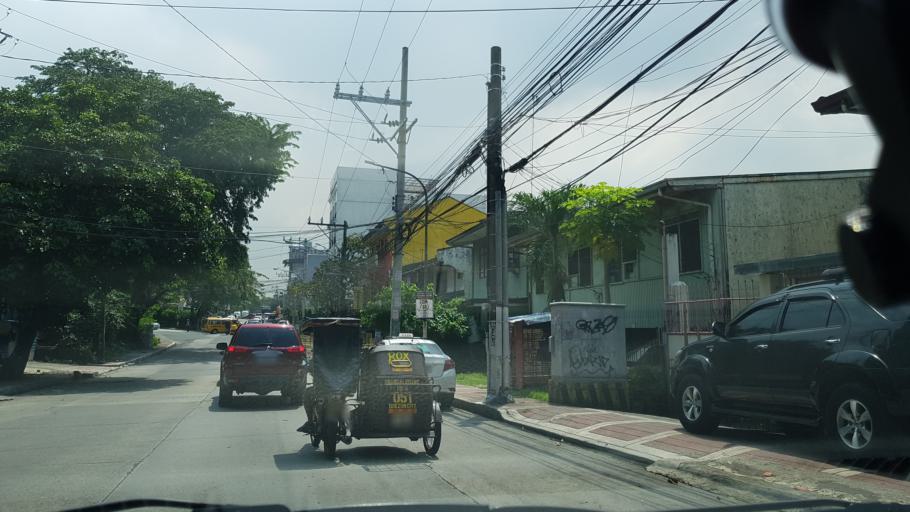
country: PH
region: Calabarzon
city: Del Monte
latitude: 14.6301
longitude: 121.0178
